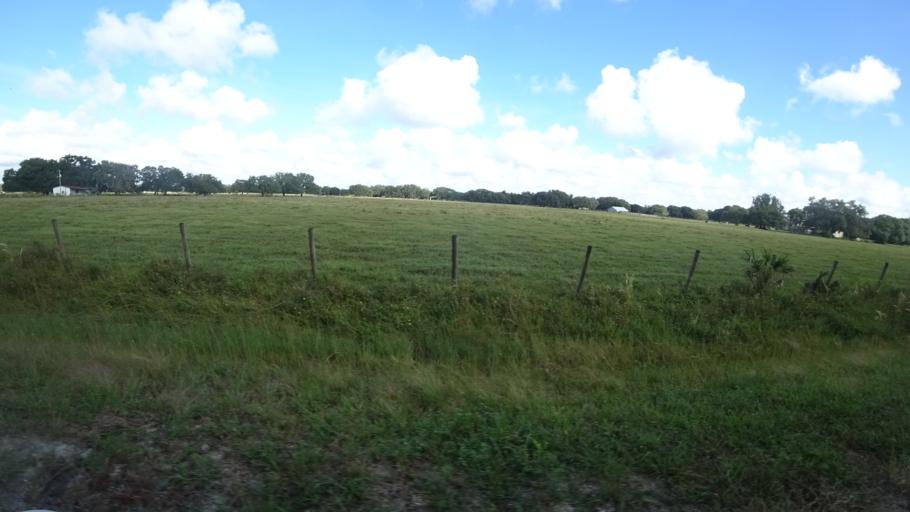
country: US
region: Florida
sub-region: Sarasota County
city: Lake Sarasota
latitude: 27.3068
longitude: -82.2223
